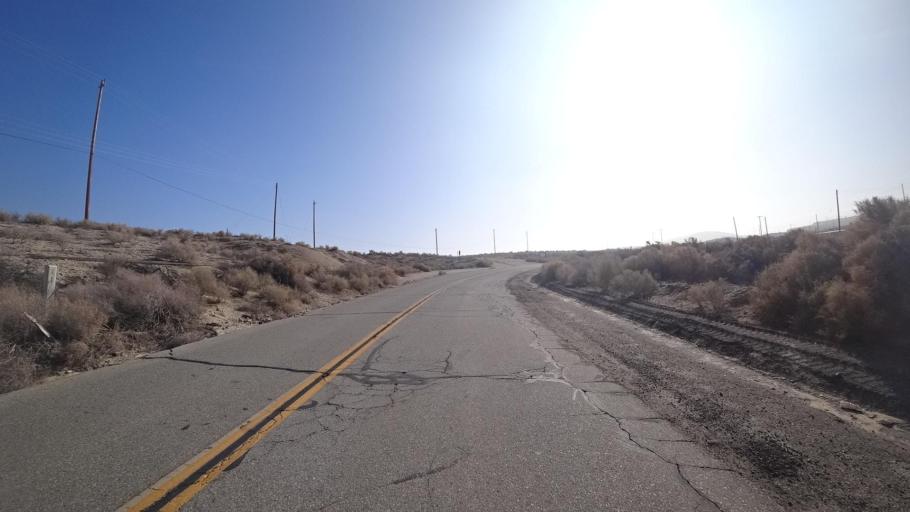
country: US
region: California
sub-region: Kern County
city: Taft Heights
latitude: 35.1493
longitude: -119.5152
